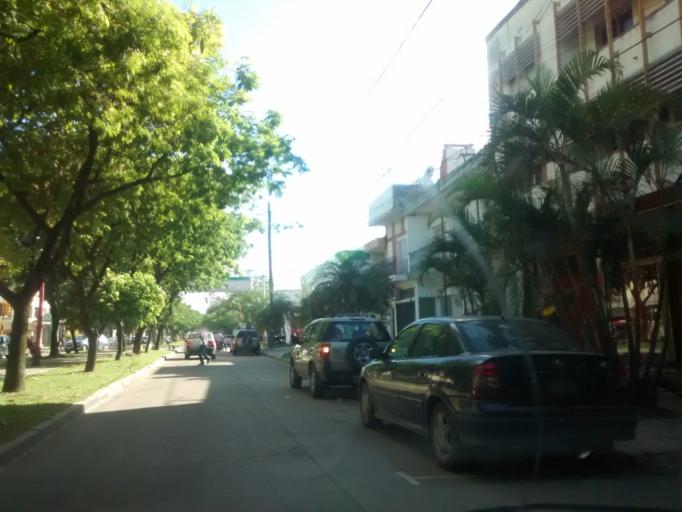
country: AR
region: Chaco
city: Resistencia
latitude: -27.4571
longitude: -58.9843
